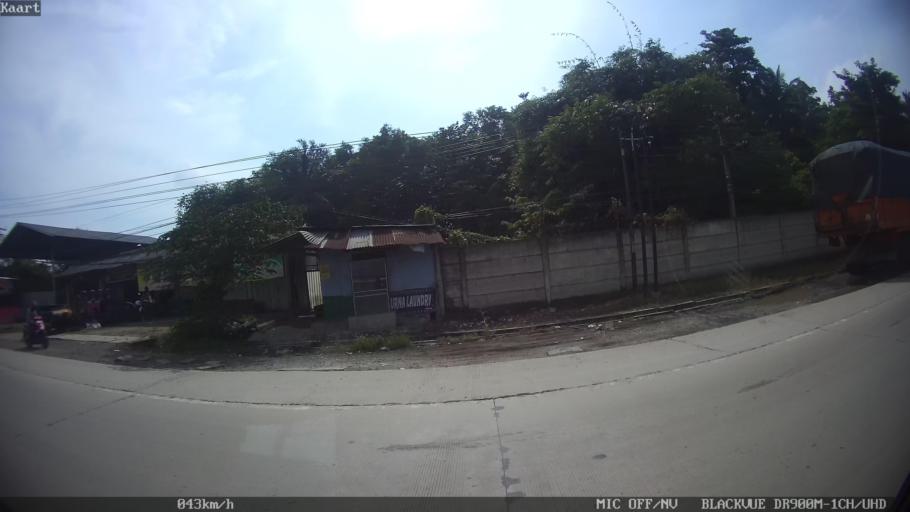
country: ID
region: Lampung
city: Kedaton
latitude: -5.4003
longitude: 105.2901
